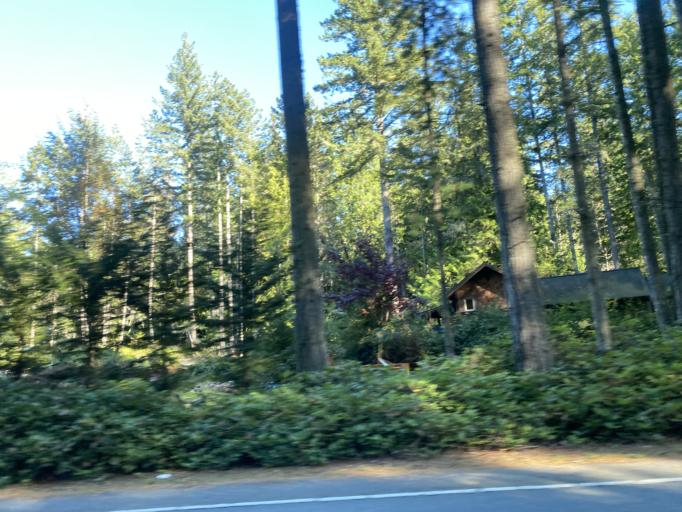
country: US
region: Washington
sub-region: Island County
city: Langley
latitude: 48.0064
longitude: -122.4254
